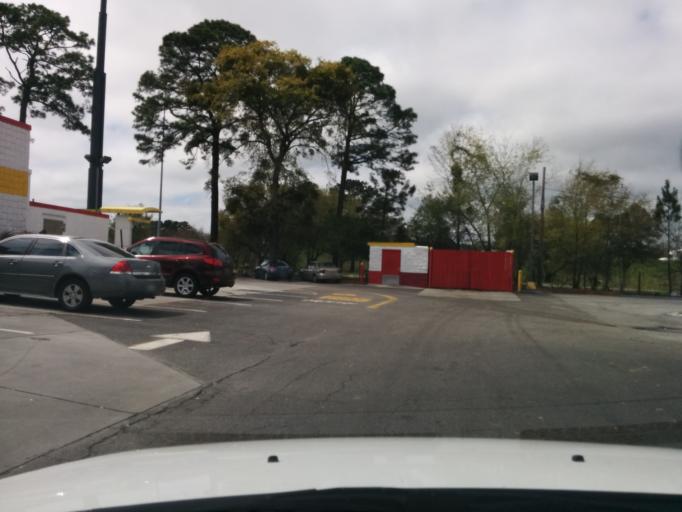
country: US
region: Georgia
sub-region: Chatham County
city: Georgetown
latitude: 32.0048
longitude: -81.2812
